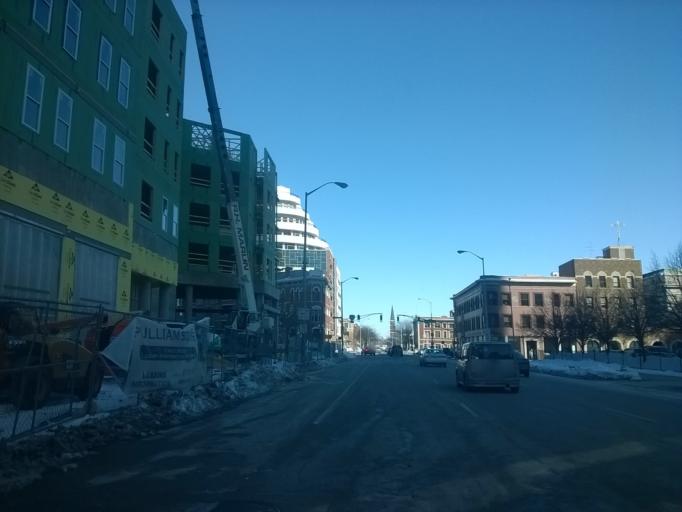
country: US
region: Indiana
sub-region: Marion County
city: Indianapolis
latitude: 39.7713
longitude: -86.1552
